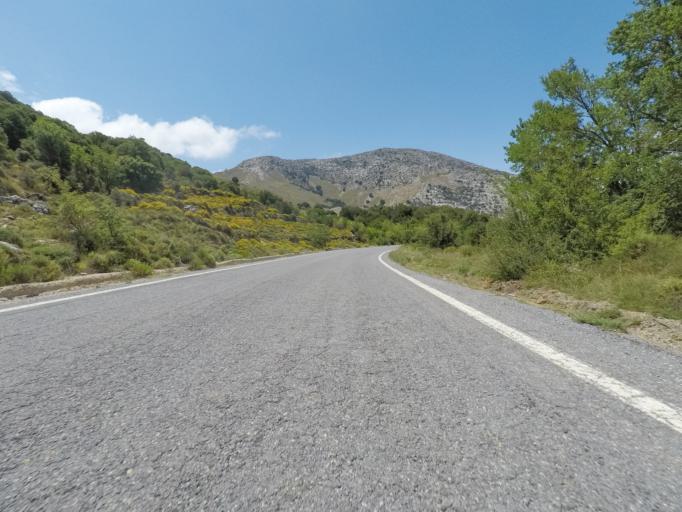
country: GR
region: Crete
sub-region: Nomos Irakleiou
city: Mokhos
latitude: 35.1783
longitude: 25.4349
